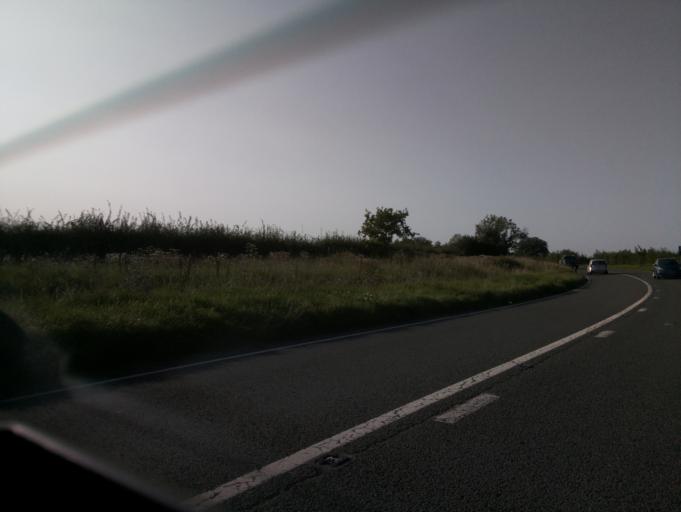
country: GB
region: England
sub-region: Gloucestershire
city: Gloucester
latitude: 51.8970
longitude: -2.2833
